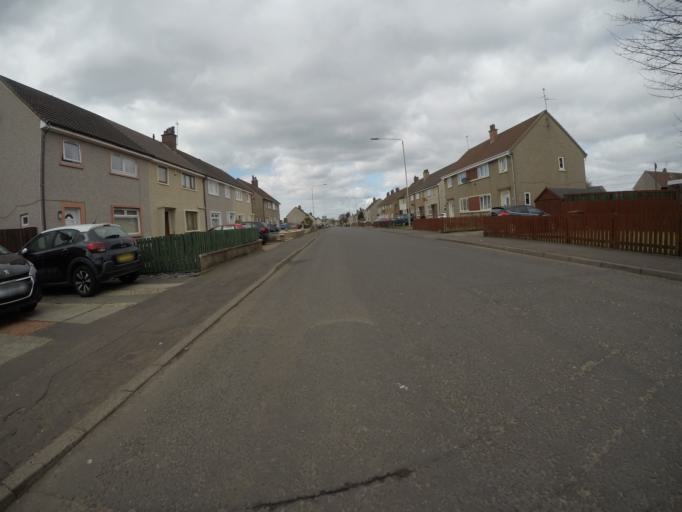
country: GB
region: Scotland
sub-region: North Ayrshire
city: Irvine
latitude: 55.6226
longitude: -4.6548
